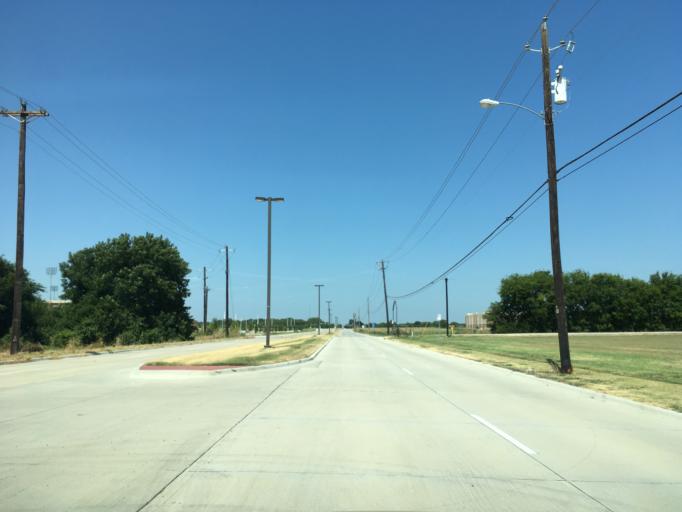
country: US
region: Texas
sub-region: Collin County
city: Fairview
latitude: 33.1591
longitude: -96.6559
